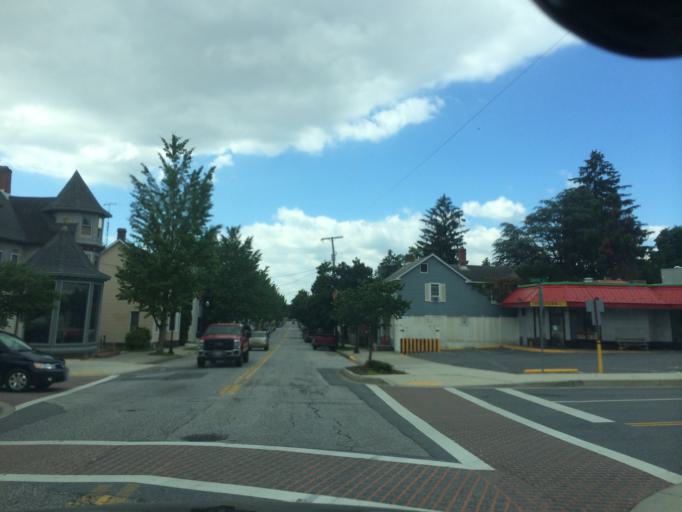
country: US
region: Maryland
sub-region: Carroll County
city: Westminster
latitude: 39.5829
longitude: -76.9990
